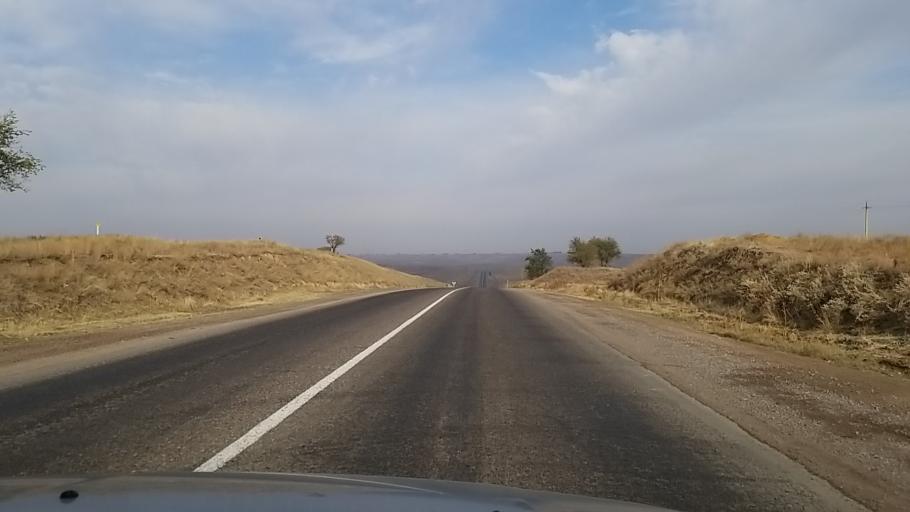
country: KZ
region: Almaty Oblysy
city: Burunday
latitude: 43.4865
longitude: 76.6713
